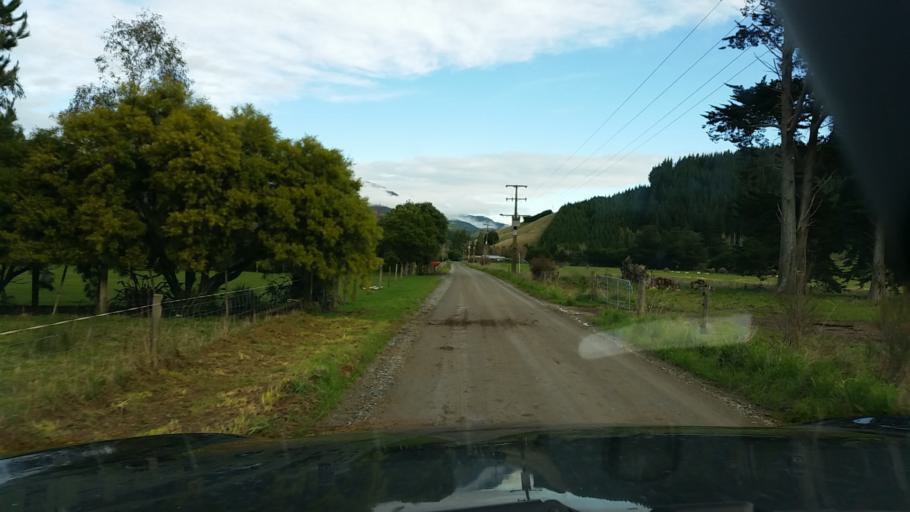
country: NZ
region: Marlborough
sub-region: Marlborough District
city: Picton
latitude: -41.3157
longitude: 173.9683
